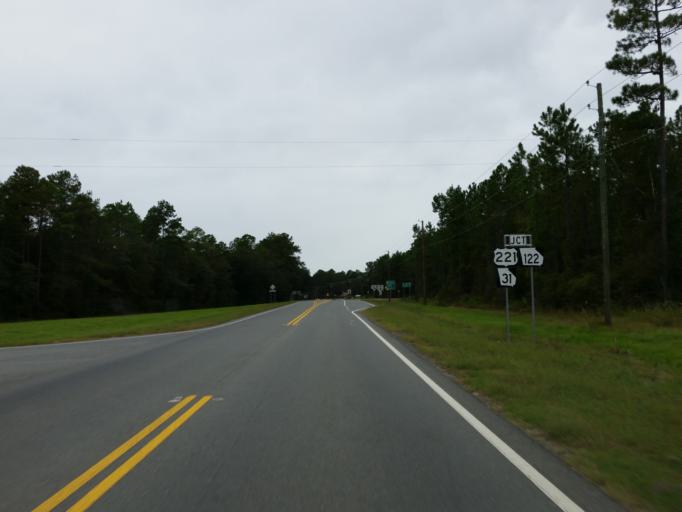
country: US
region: Georgia
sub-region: Lanier County
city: Lakeland
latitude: 31.0479
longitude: -83.0294
